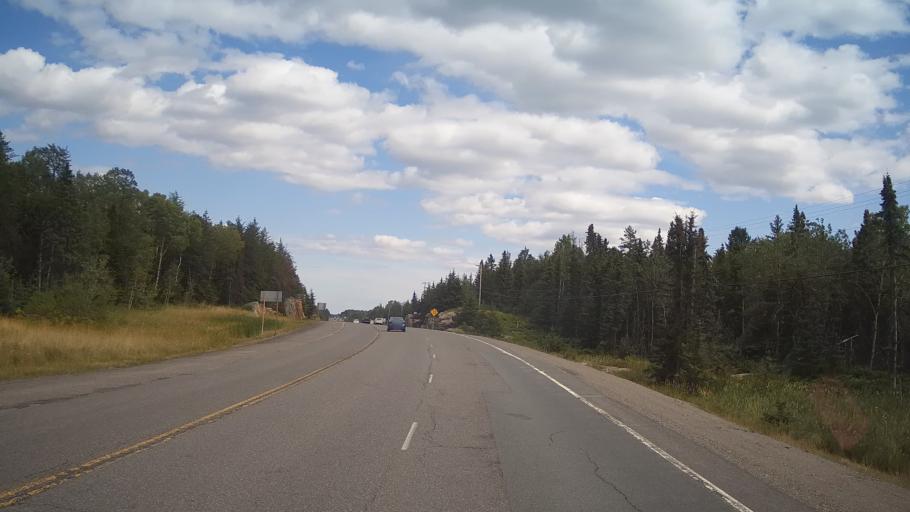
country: CA
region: Ontario
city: Greater Sudbury
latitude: 46.4796
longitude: -80.5434
